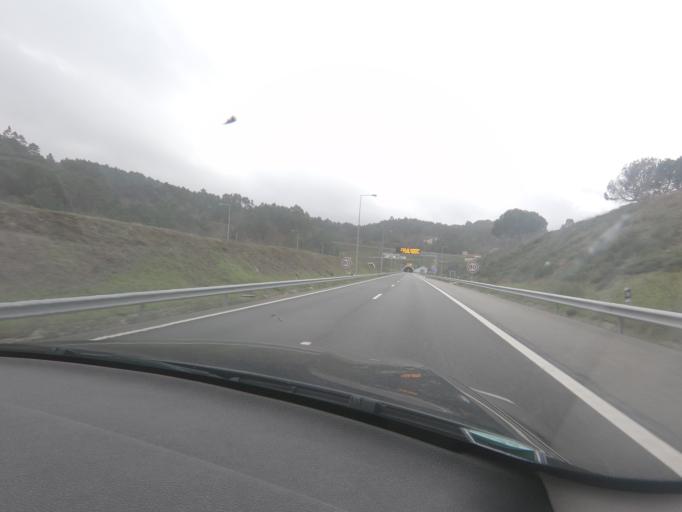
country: PT
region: Viseu
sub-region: Castro Daire
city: Castro Daire
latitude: 40.9012
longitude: -7.9125
